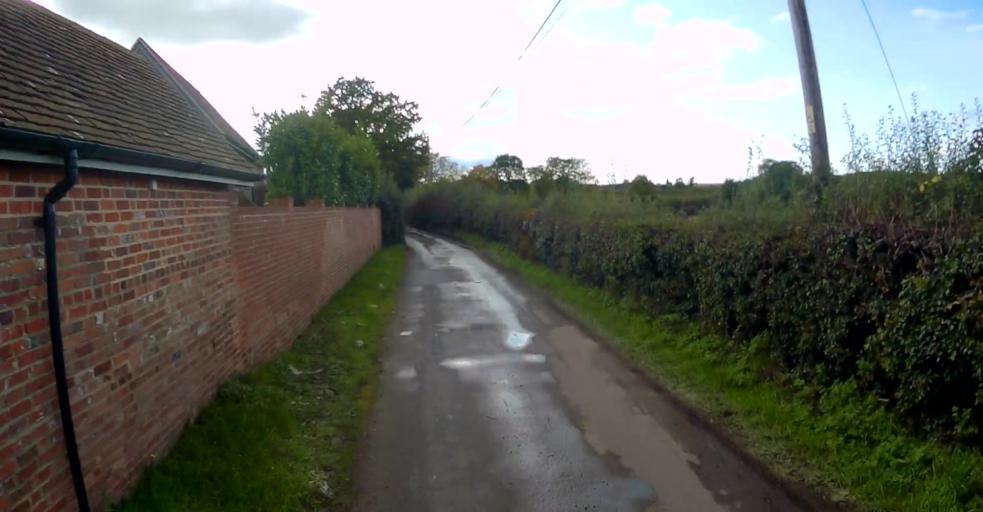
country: GB
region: England
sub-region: Surrey
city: Farnham
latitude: 51.2069
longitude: -0.8441
